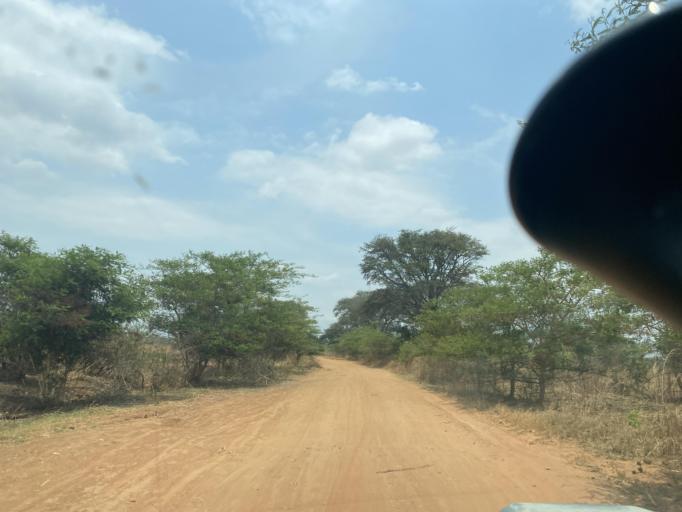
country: ZM
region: Lusaka
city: Chongwe
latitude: -15.5229
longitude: 28.8225
